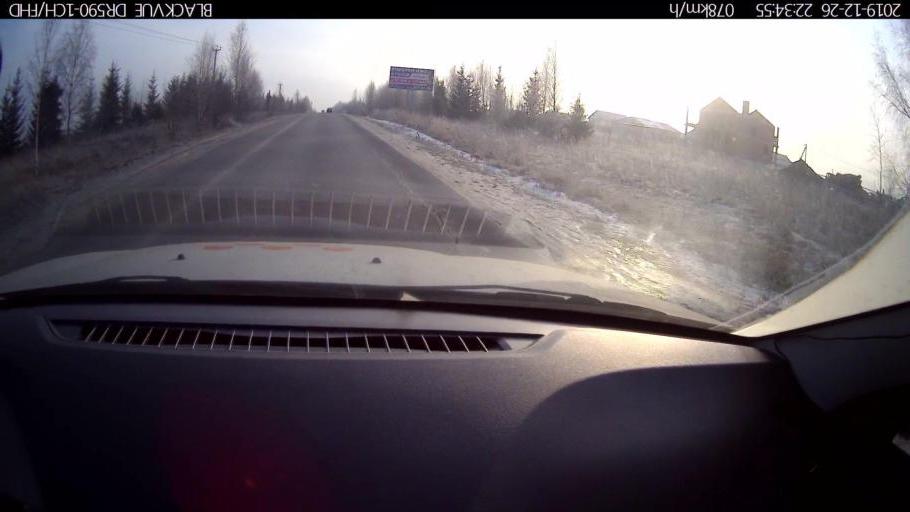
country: RU
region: Nizjnij Novgorod
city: Burevestnik
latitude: 56.1518
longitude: 43.7147
